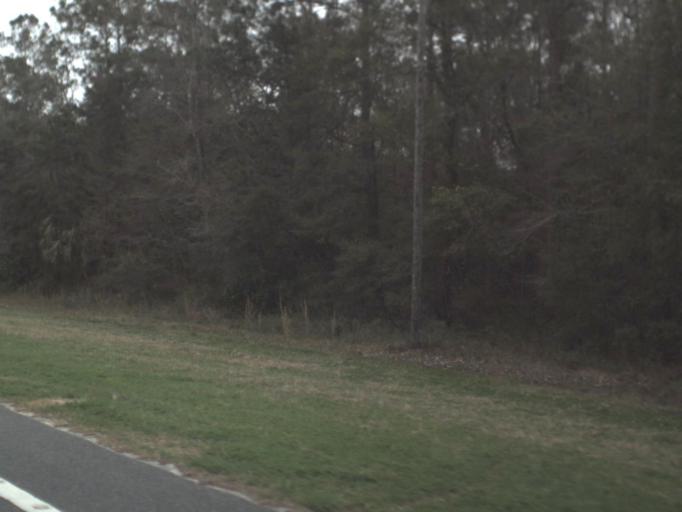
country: US
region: Florida
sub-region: Wakulla County
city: Crawfordville
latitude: 30.1713
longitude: -84.2476
